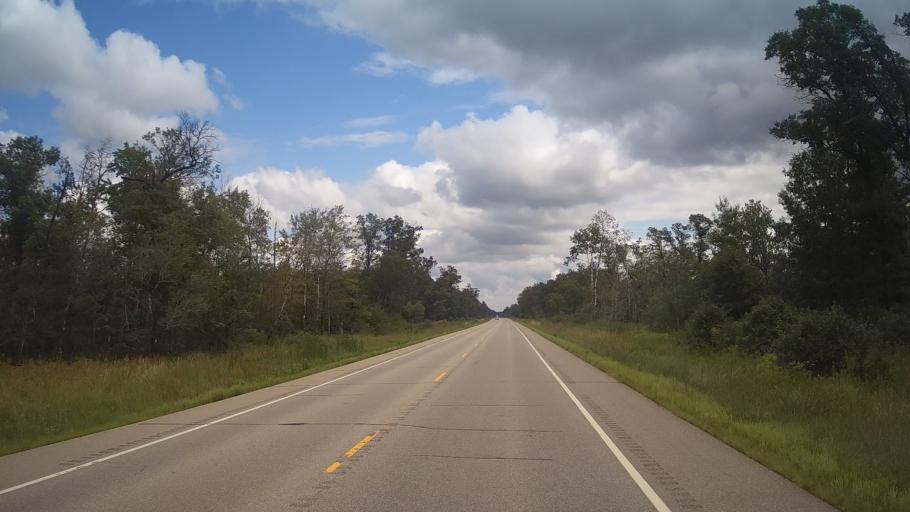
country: US
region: Wisconsin
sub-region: Adams County
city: Friendship
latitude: 44.0254
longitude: -89.7214
